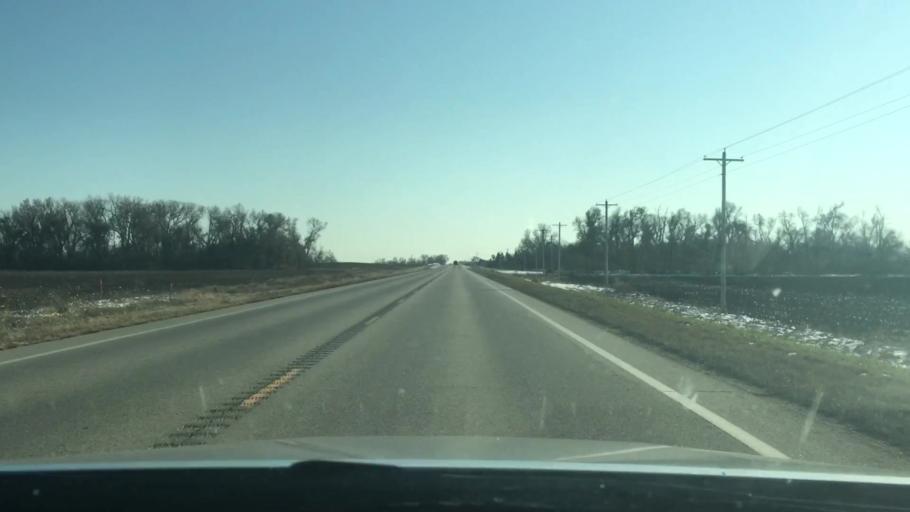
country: US
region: Kansas
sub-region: Rice County
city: Lyons
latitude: 38.3104
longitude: -98.2018
